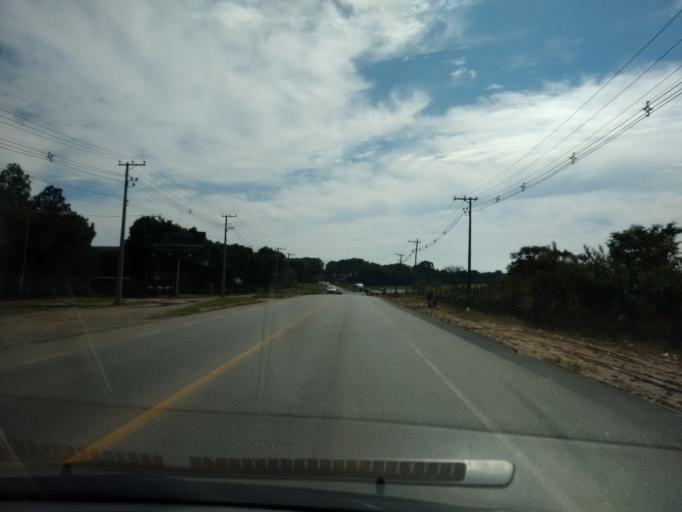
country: BR
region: Sao Paulo
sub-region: Itu
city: Itu
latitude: -23.3023
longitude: -47.3035
